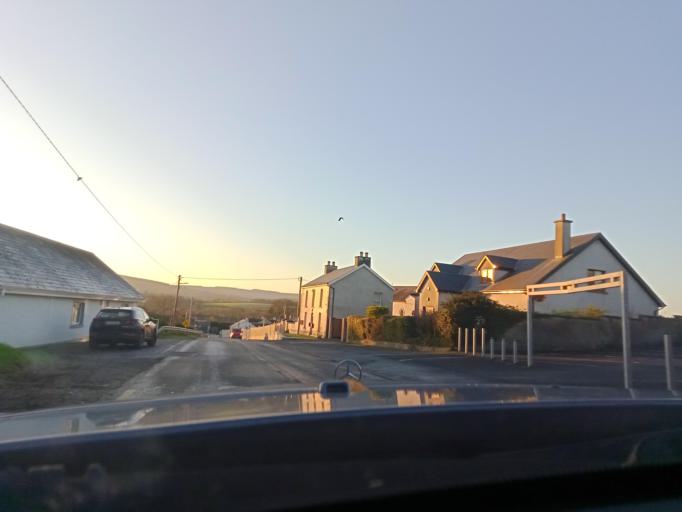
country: IE
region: Leinster
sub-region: Kilkenny
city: Mooncoin
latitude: 52.3683
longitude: -7.1670
